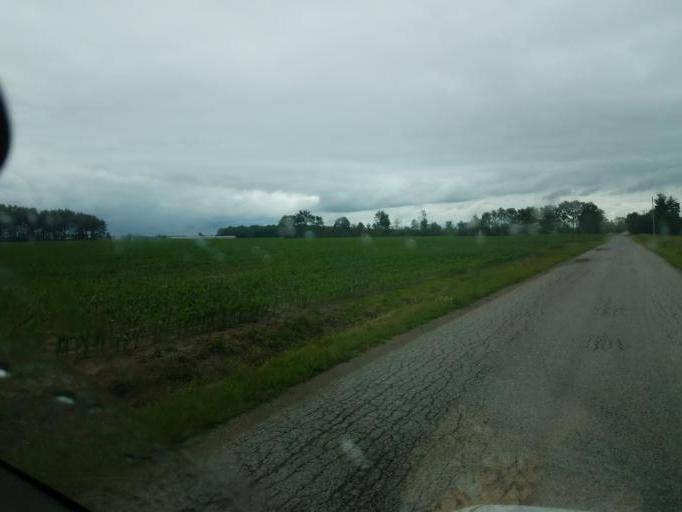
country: US
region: Ohio
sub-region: Morrow County
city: Cardington
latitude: 40.5281
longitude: -82.8995
